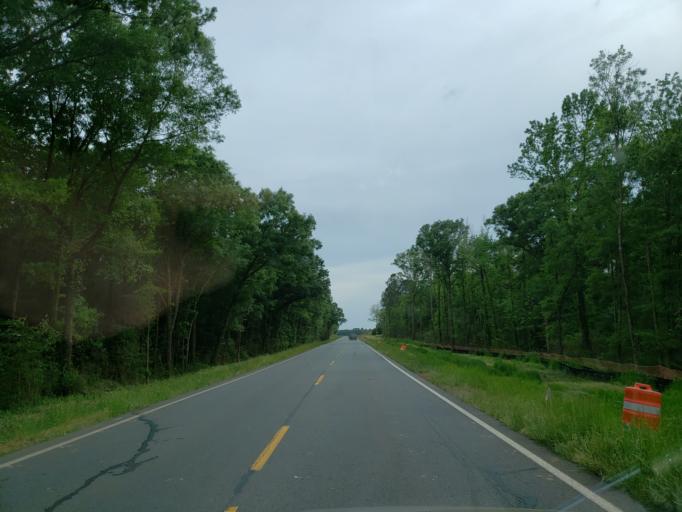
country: US
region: Georgia
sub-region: Macon County
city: Marshallville
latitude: 32.3748
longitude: -83.8898
